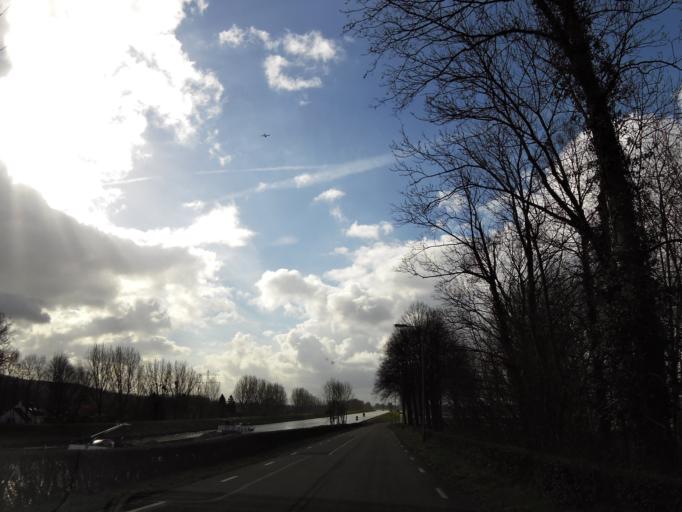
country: NL
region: Limburg
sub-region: Gemeente Meerssen
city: Meerssen
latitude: 50.9232
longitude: 5.7400
